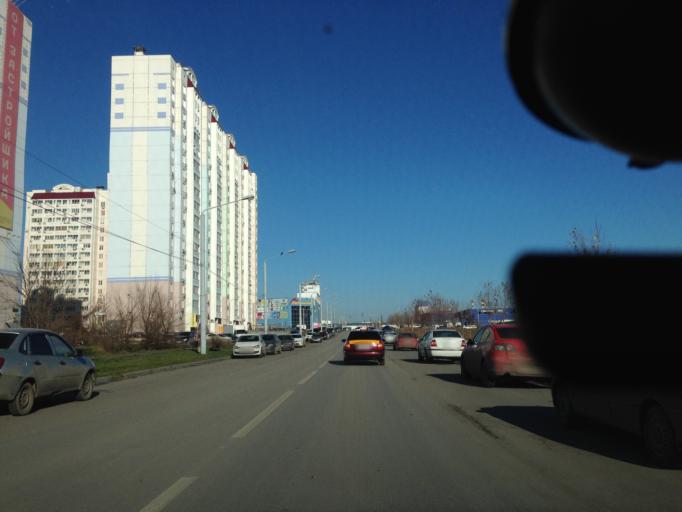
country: RU
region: Rostov
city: Kalinin
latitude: 47.2329
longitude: 39.6053
